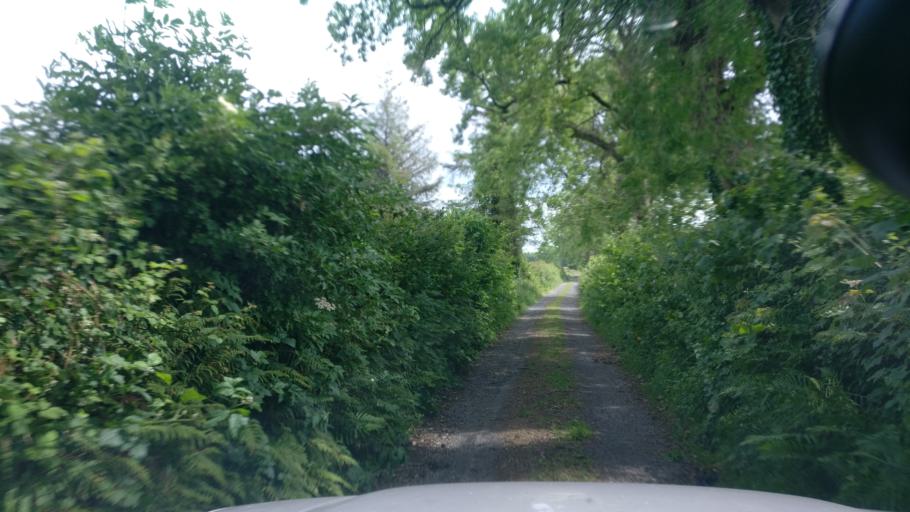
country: IE
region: Connaught
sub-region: County Galway
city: Ballinasloe
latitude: 53.2697
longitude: -8.3323
